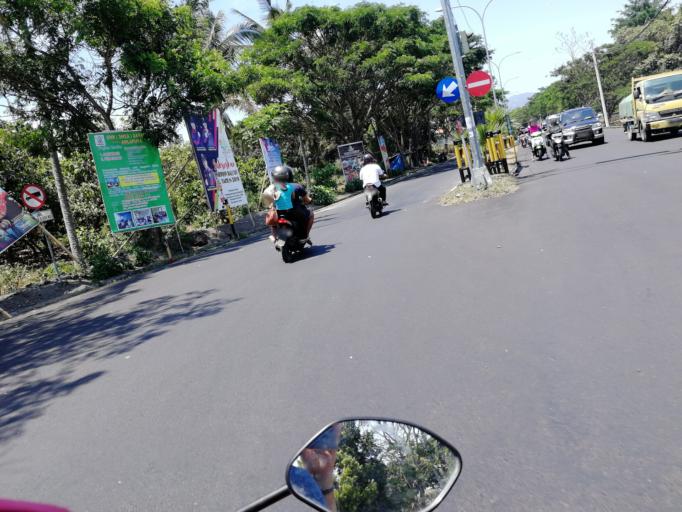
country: ID
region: Bali
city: Banjar Beji
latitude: -8.4473
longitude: 115.5876
